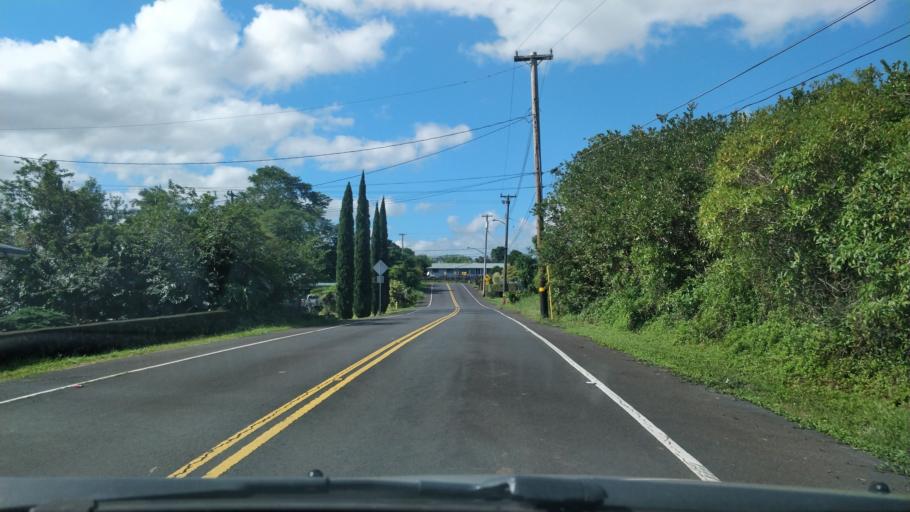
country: US
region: Hawaii
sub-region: Hawaii County
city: Hilo
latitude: 19.6819
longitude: -155.1051
